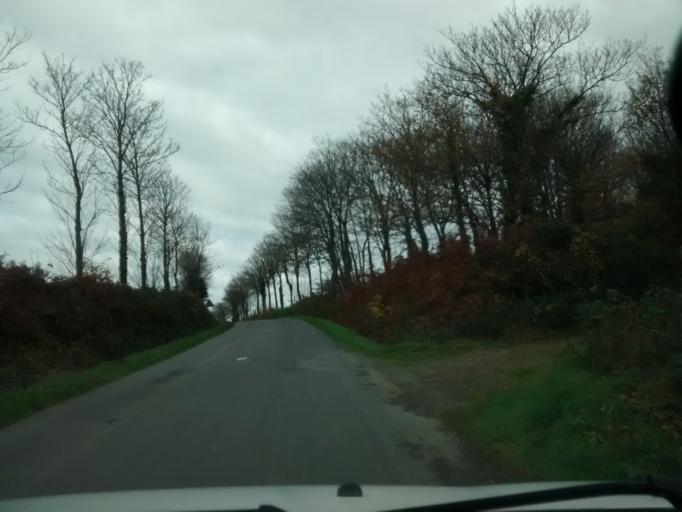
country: FR
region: Brittany
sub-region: Departement d'Ille-et-Vilaine
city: Argentre-du-Plessis
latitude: 48.0760
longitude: -1.1637
